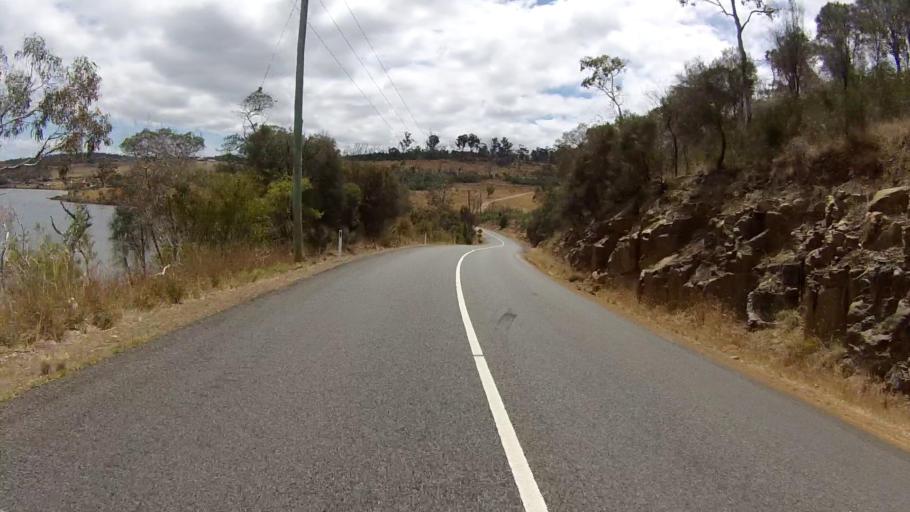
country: AU
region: Tasmania
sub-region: Sorell
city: Sorell
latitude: -42.8650
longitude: 147.6916
